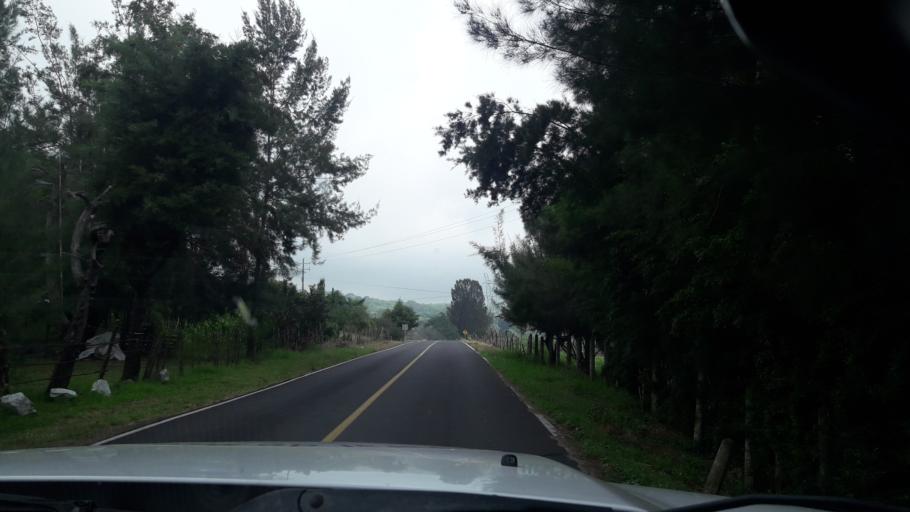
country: MX
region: Colima
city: Queseria
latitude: 19.4101
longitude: -103.6433
